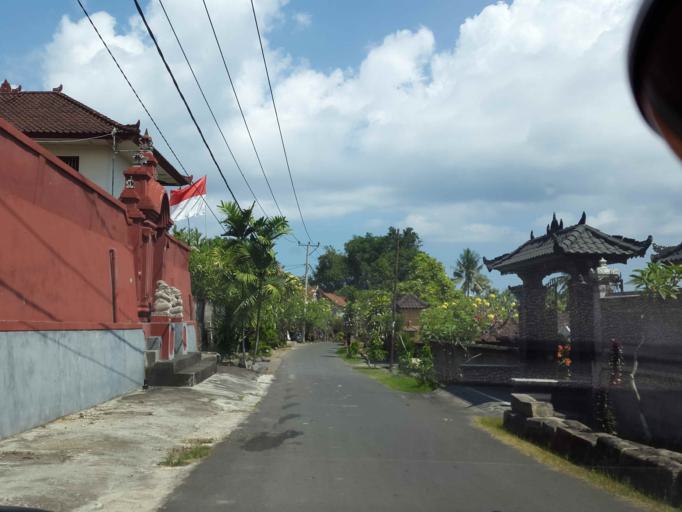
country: ID
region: Bali
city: Klungkung
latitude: -8.5610
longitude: 115.3814
